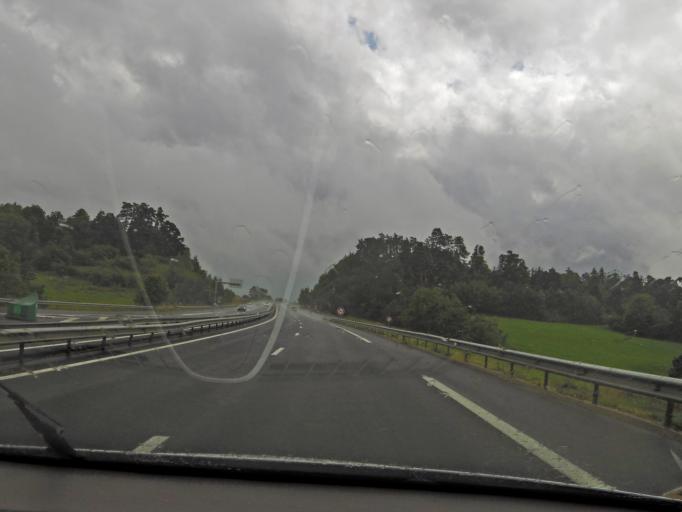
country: FR
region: Auvergne
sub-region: Departement du Cantal
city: Saint-Flour
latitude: 45.0502
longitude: 3.1121
